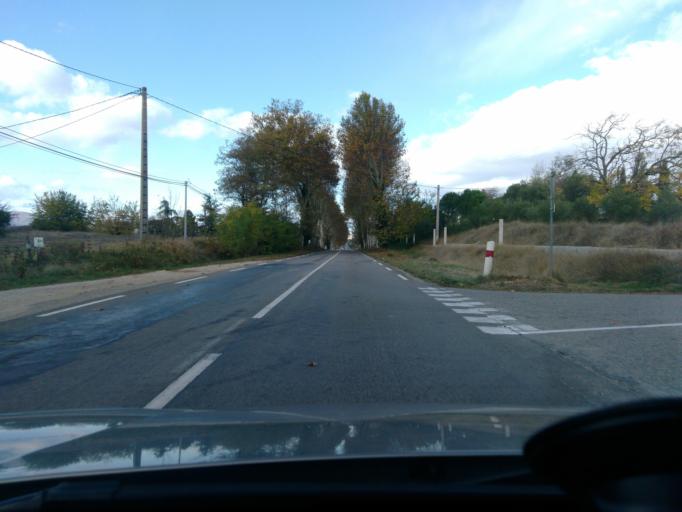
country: FR
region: Rhone-Alpes
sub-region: Departement de la Drome
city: Malataverne
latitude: 44.4940
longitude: 4.7431
